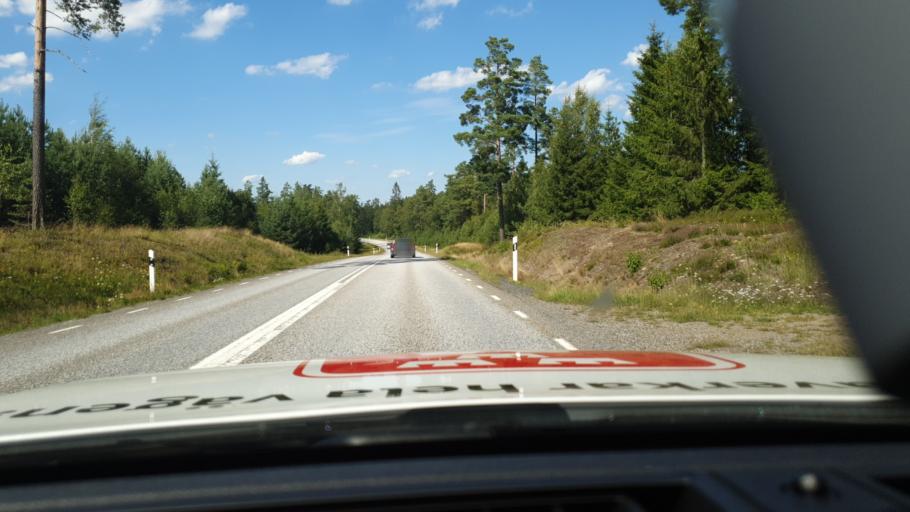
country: SE
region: Joenkoeping
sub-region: Vaggeryds Kommun
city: Vaggeryd
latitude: 57.6005
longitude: 14.2201
